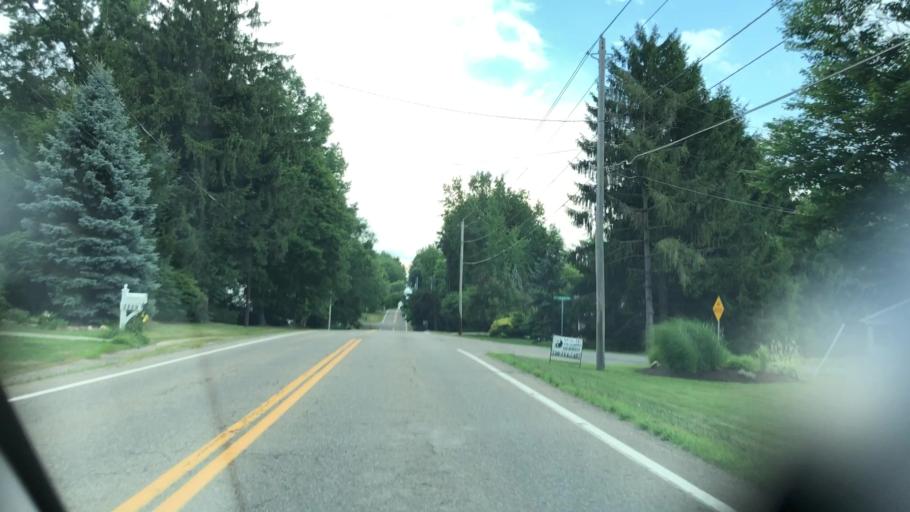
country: US
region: Ohio
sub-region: Summit County
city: Barberton
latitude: 41.0085
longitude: -81.5679
